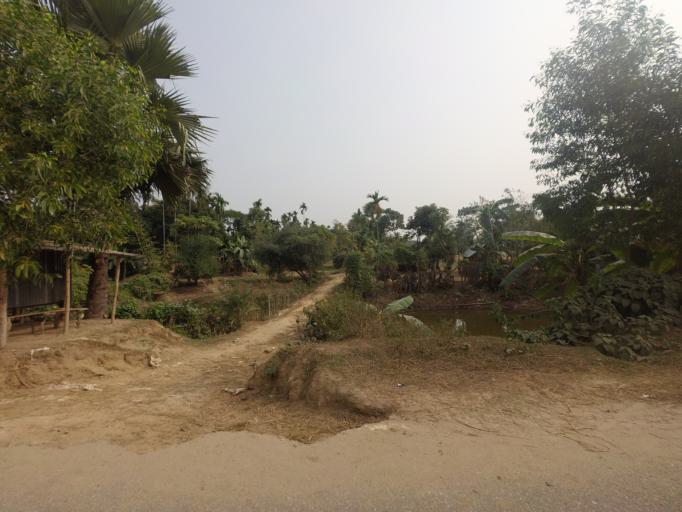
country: BD
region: Dhaka
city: Netrakona
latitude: 25.1441
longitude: 90.6597
